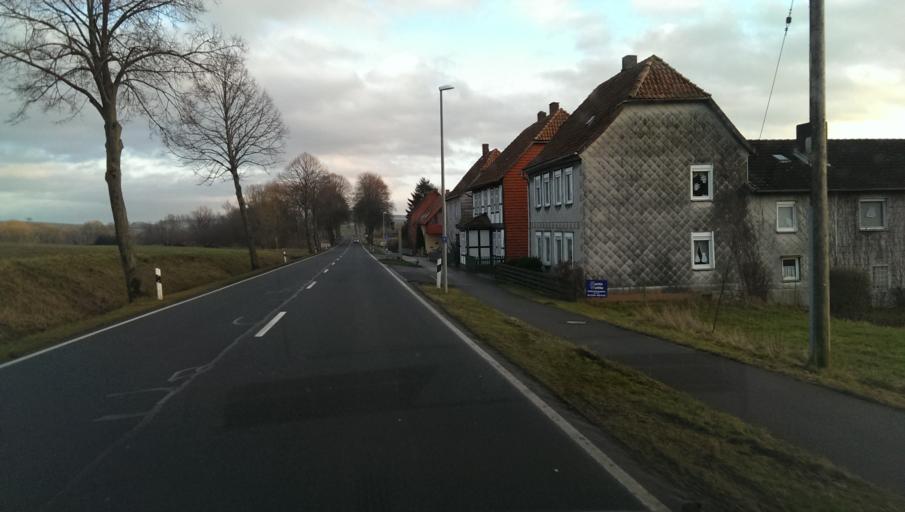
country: DE
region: Lower Saxony
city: Eimen
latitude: 51.8783
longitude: 9.7837
